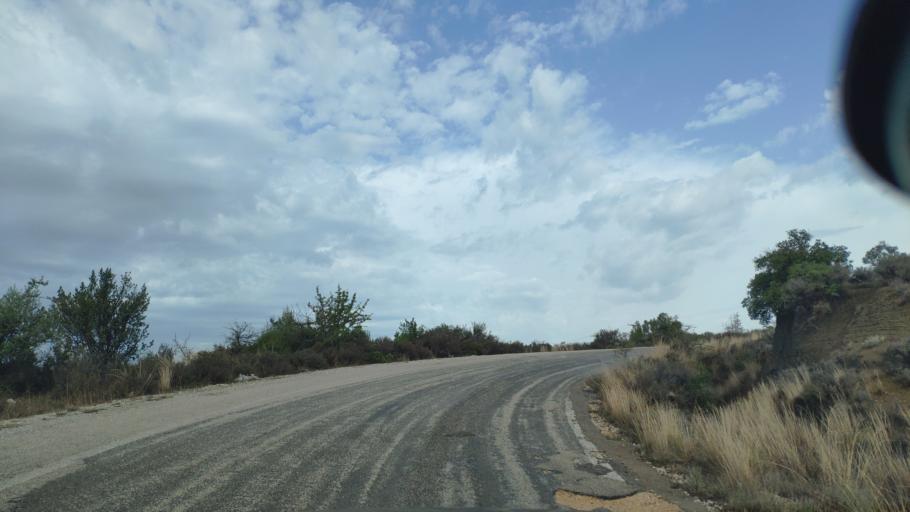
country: GR
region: West Greece
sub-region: Nomos Aitolias kai Akarnanias
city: Sardinia
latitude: 38.8751
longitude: 21.2571
